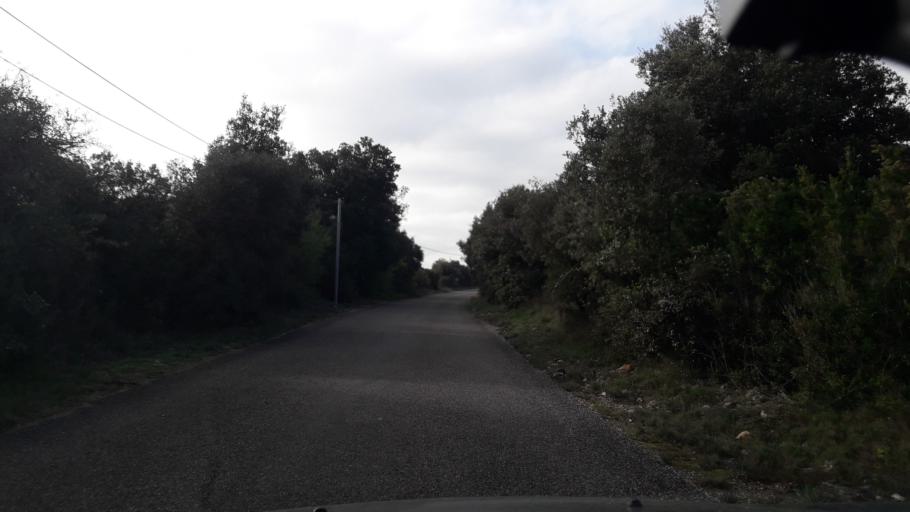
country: FR
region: Languedoc-Roussillon
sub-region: Departement du Gard
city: Saint-Julien-de-Peyrolas
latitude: 44.3558
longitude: 4.5296
